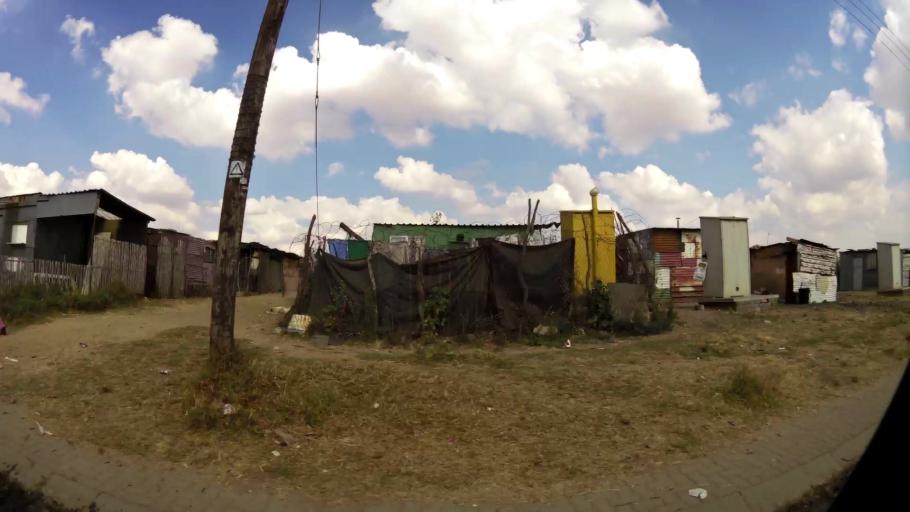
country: ZA
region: Gauteng
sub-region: City of Johannesburg Metropolitan Municipality
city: Roodepoort
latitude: -26.1843
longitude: 27.8484
